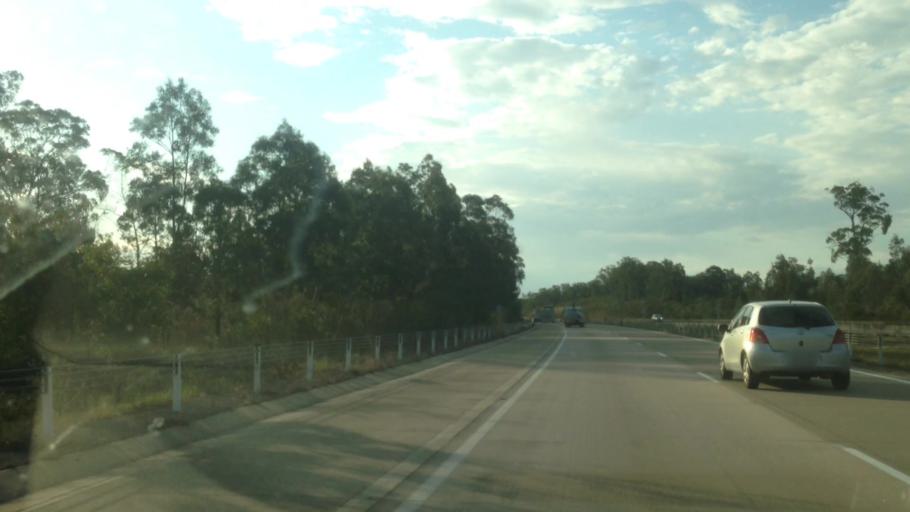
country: AU
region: New South Wales
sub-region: Cessnock
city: Heddon Greta
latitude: -32.8352
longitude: 151.5380
